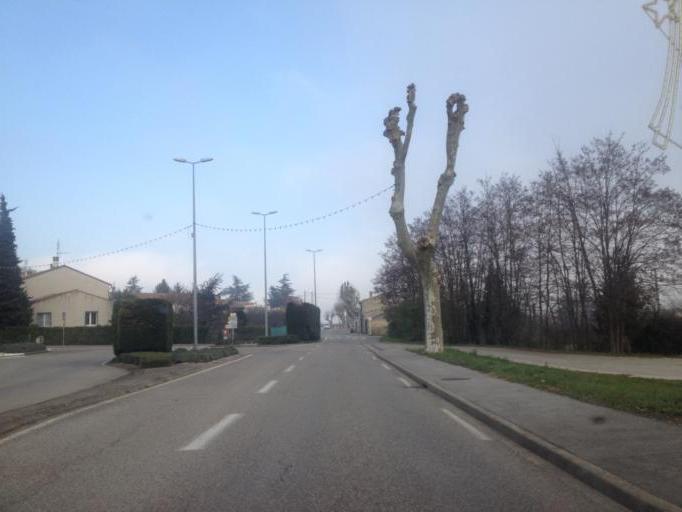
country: FR
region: Rhone-Alpes
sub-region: Departement de l'Ardeche
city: Saint-Jean-de-Muzols
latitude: 45.0847
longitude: 4.8162
